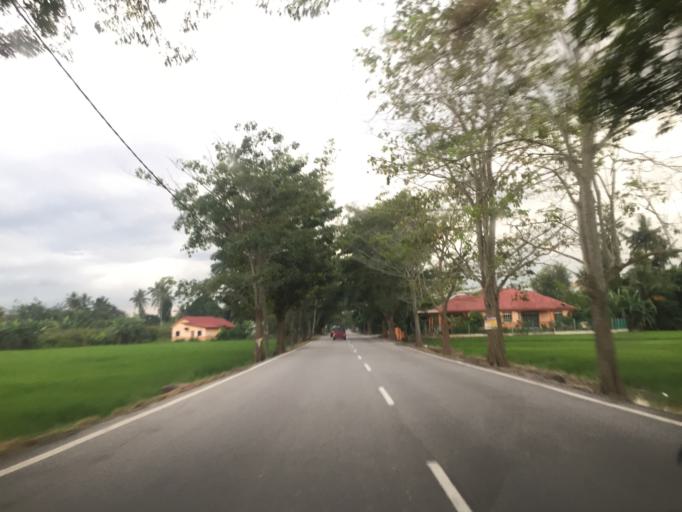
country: MY
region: Penang
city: Tasek Glugor
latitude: 5.5482
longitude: 100.5054
